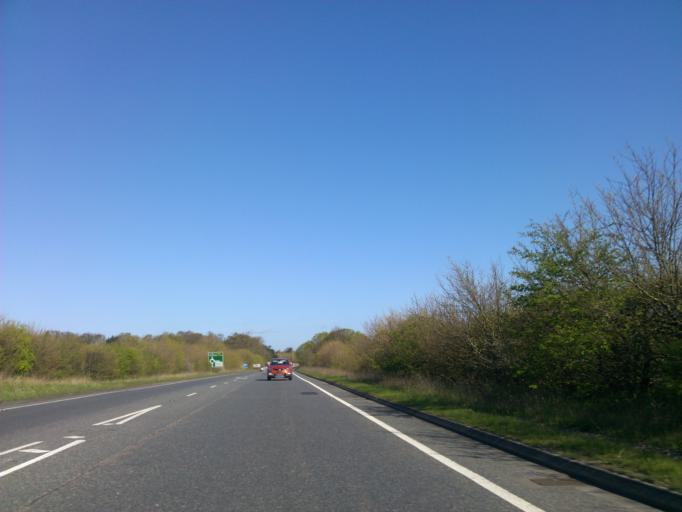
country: GB
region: England
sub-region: Essex
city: Little Clacton
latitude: 51.8157
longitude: 1.1404
